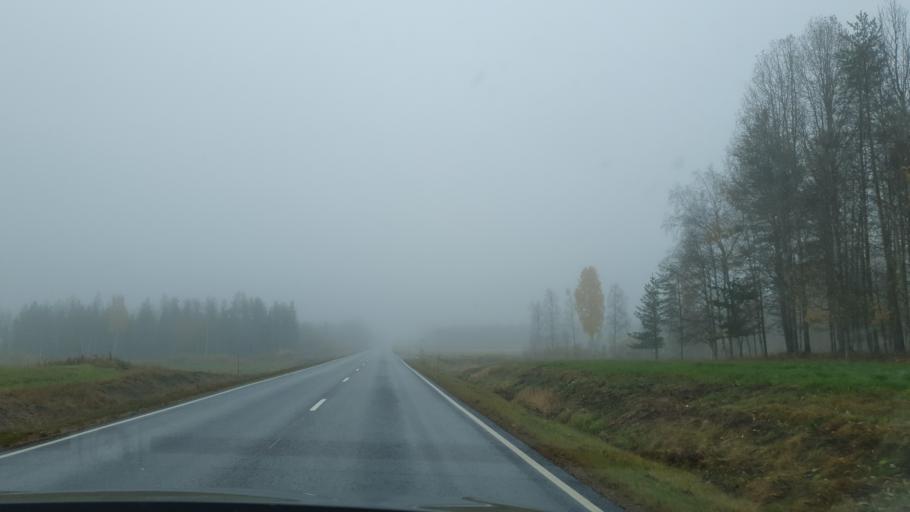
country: FI
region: Lapland
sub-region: Rovaniemi
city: Rovaniemi
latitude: 66.7998
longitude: 25.4141
